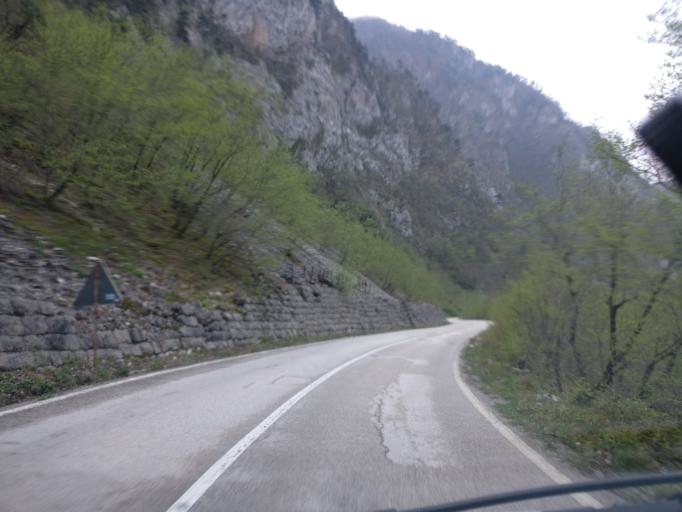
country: ME
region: Opstina Pluzine
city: Pluzine
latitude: 43.3009
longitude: 18.8522
